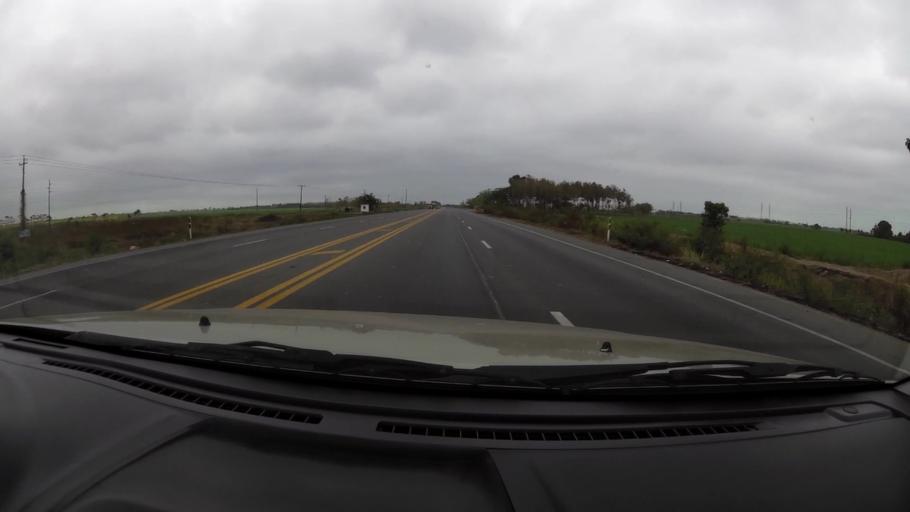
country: EC
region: Guayas
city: Naranjal
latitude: -2.4745
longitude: -79.6201
